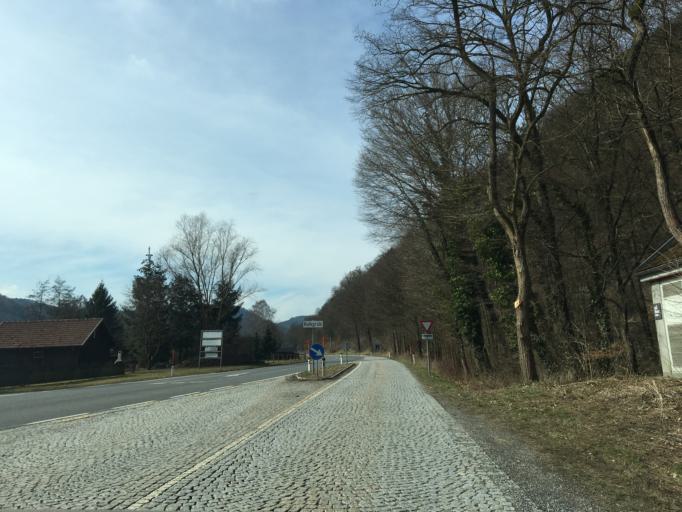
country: AT
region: Lower Austria
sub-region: Politischer Bezirk Melk
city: Nochling
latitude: 48.1967
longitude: 14.9986
